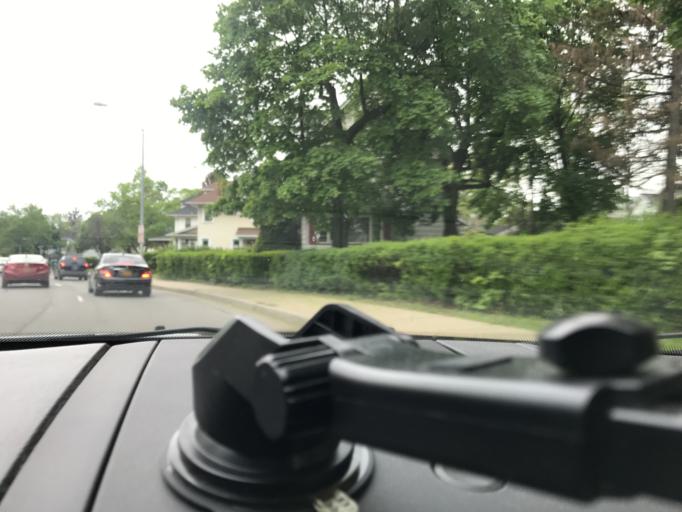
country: US
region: New York
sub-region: Monroe County
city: Rochester
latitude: 43.1258
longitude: -77.6393
